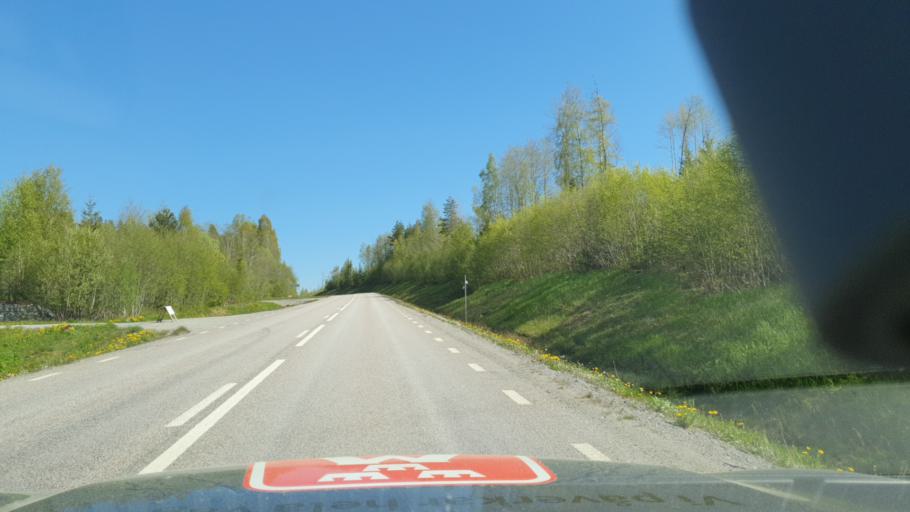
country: SE
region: Vaesternorrland
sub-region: OErnskoeldsviks Kommun
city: Ornskoldsvik
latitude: 63.3775
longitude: 18.6837
